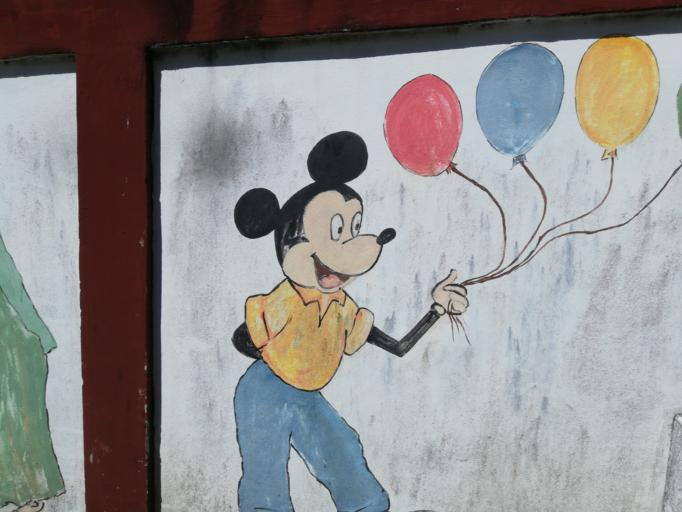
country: MU
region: Moka
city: Moka
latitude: -20.2310
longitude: 57.4982
